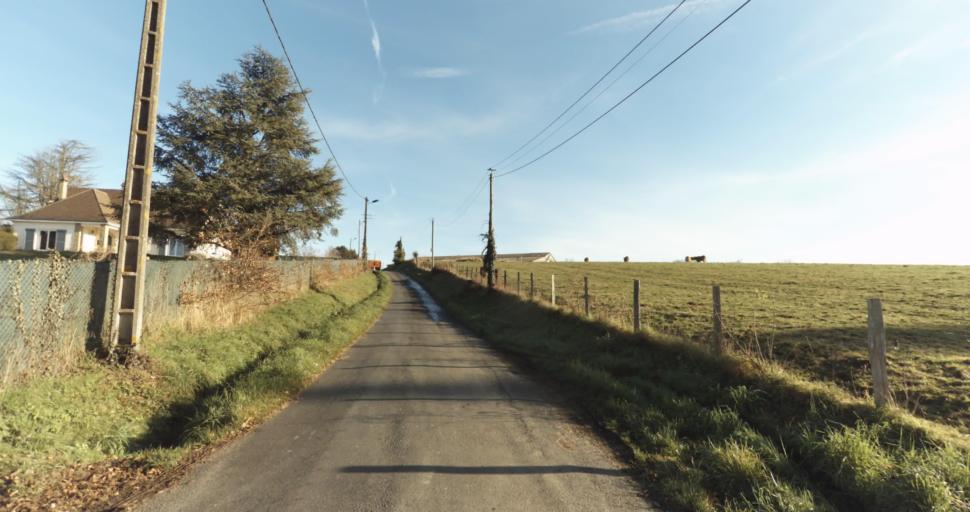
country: FR
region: Limousin
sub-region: Departement de la Haute-Vienne
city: Saint-Priest-sous-Aixe
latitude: 45.7991
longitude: 1.1113
